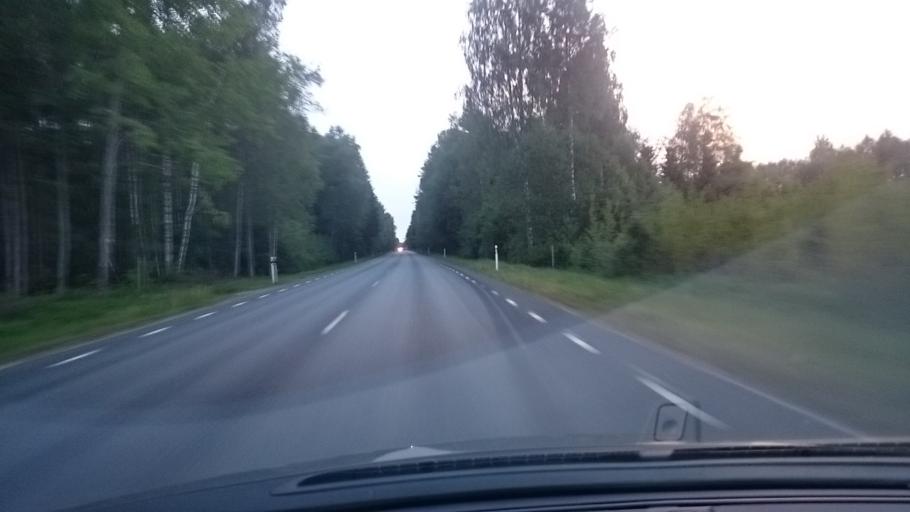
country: EE
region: Raplamaa
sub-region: Kehtna vald
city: Kehtna
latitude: 58.8451
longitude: 25.0481
